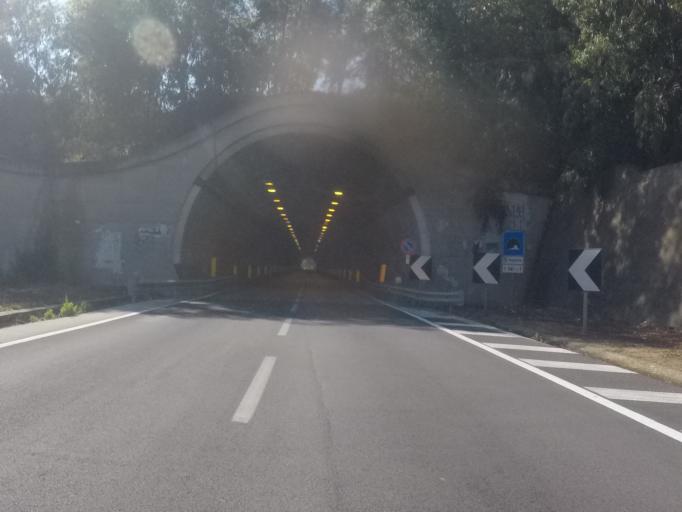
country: IT
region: Sicily
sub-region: Agrigento
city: Ribera
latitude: 37.4741
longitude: 13.2266
